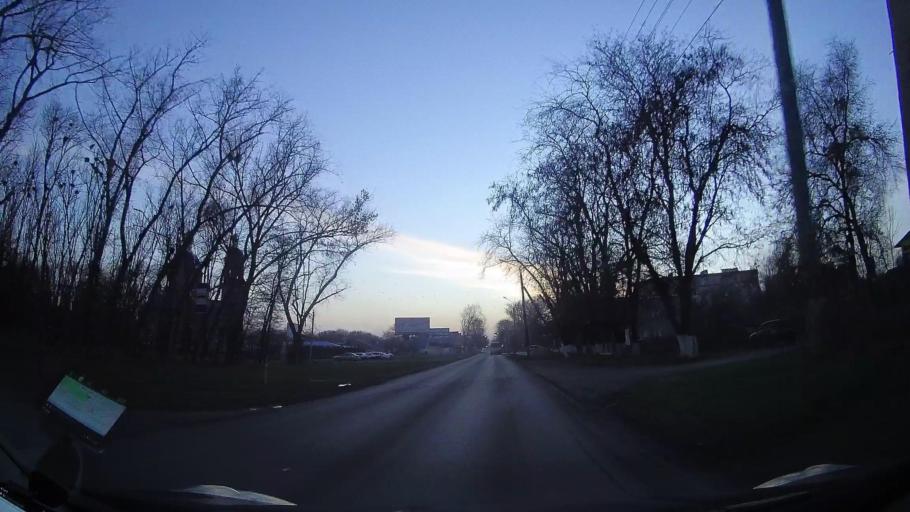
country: RU
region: Rostov
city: Zernograd
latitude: 46.8541
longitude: 40.3138
